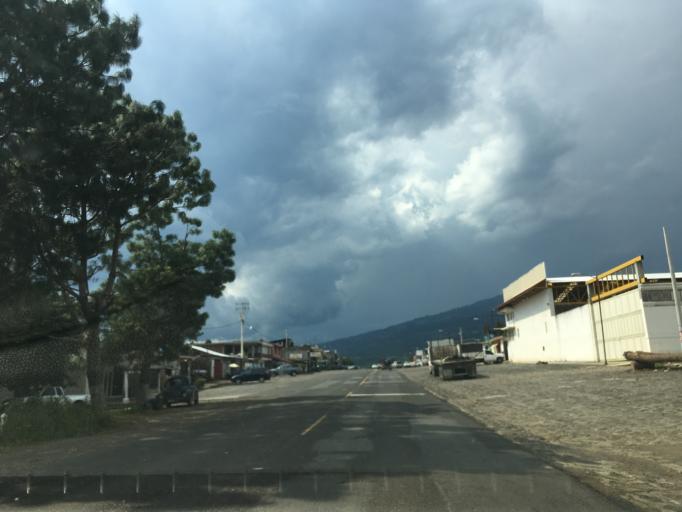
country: MX
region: Michoacan
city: Tingambato
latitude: 19.5042
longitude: -101.8480
